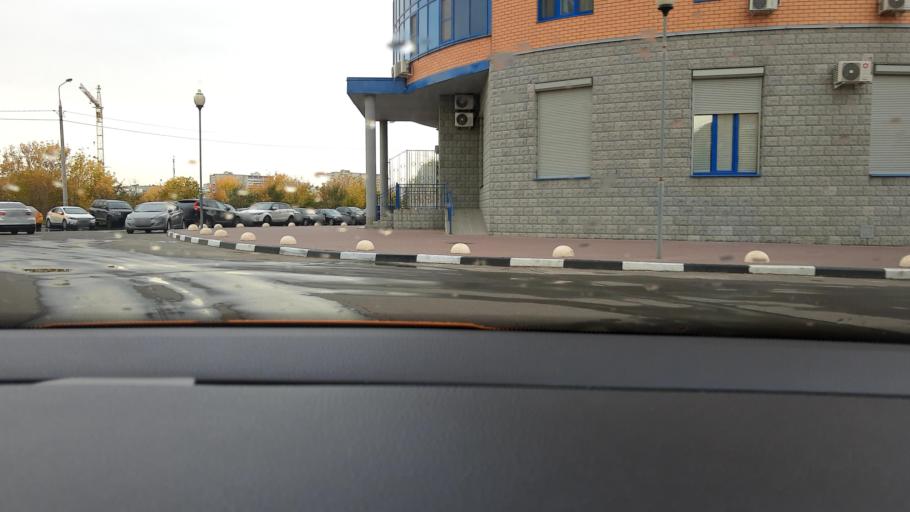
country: RU
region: Moscow
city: Ivanovskoye
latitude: 55.7731
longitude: 37.8467
